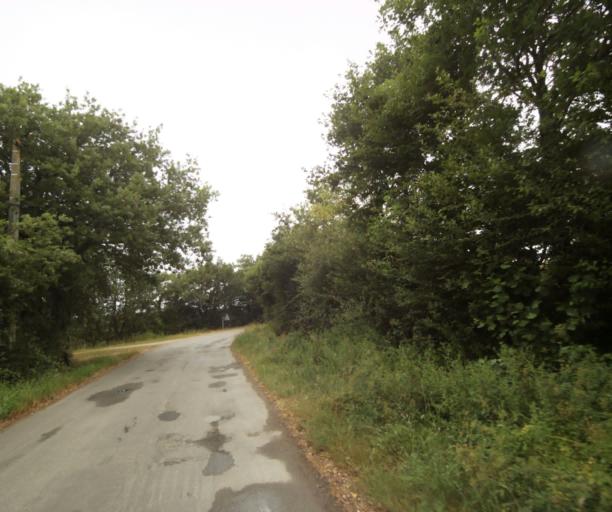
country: FR
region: Pays de la Loire
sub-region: Departement de la Vendee
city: Chateau-d'Olonne
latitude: 46.4798
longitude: -1.6884
